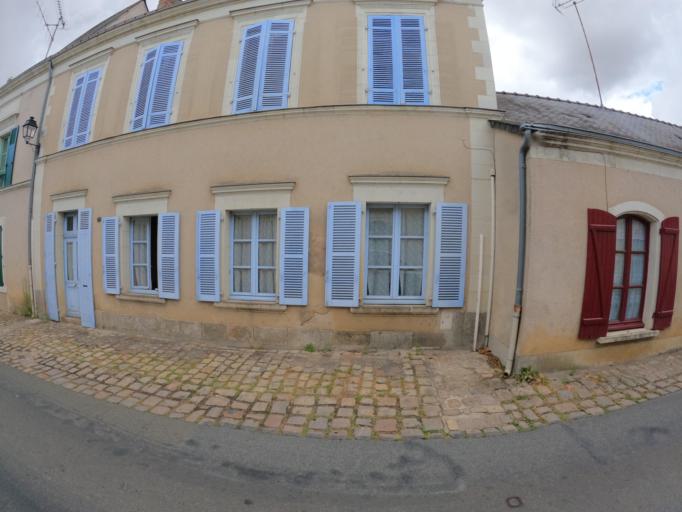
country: FR
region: Pays de la Loire
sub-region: Departement de Maine-et-Loire
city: Morannes
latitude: 47.7924
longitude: -0.4395
